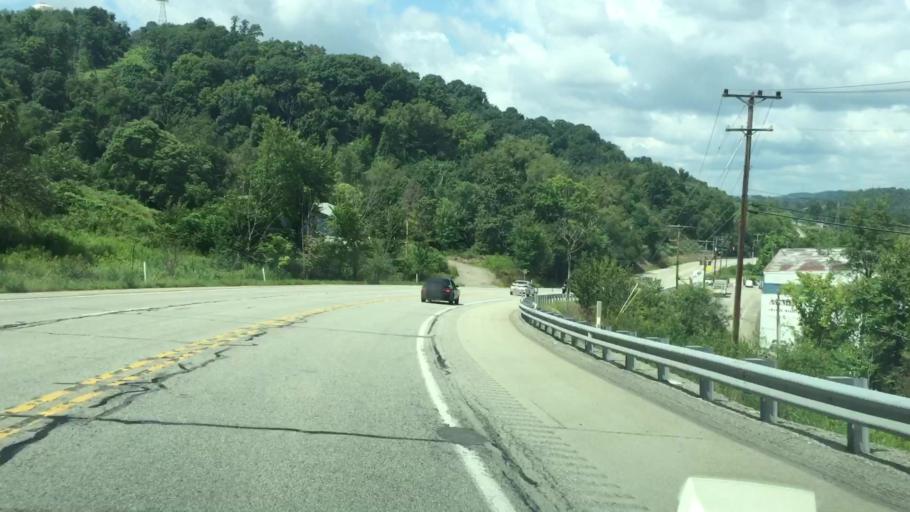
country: US
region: Pennsylvania
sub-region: Allegheny County
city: Oakmont
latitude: 40.5530
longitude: -79.8482
